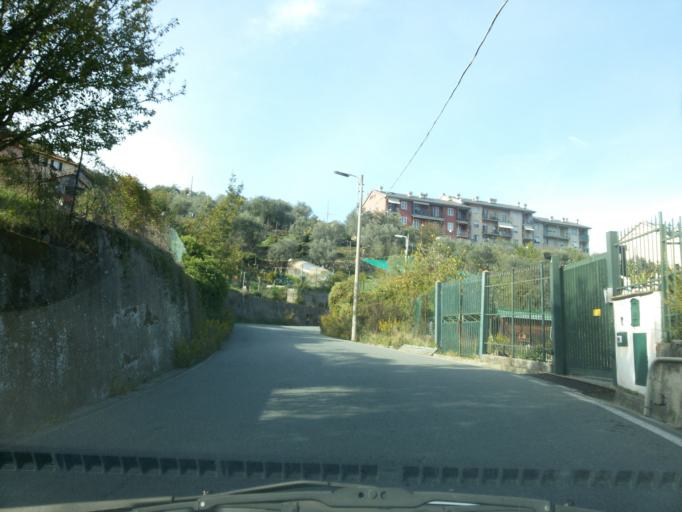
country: IT
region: Liguria
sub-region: Provincia di Genova
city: Piccarello
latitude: 44.4580
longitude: 8.9719
